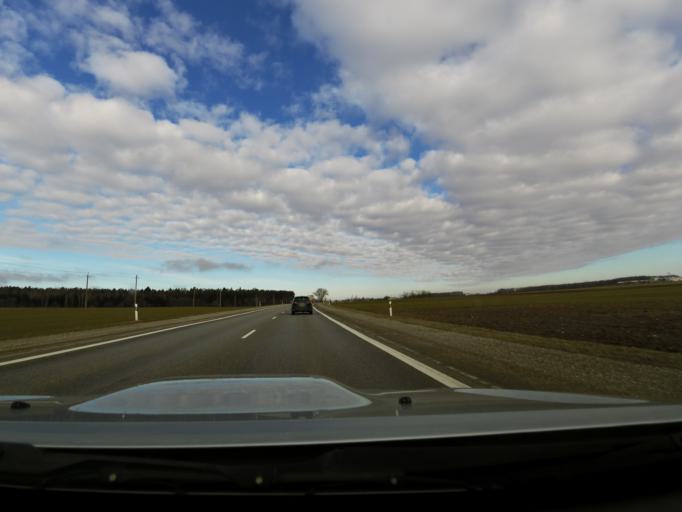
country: LT
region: Siauliu apskritis
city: Pakruojis
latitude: 55.7668
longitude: 24.0681
